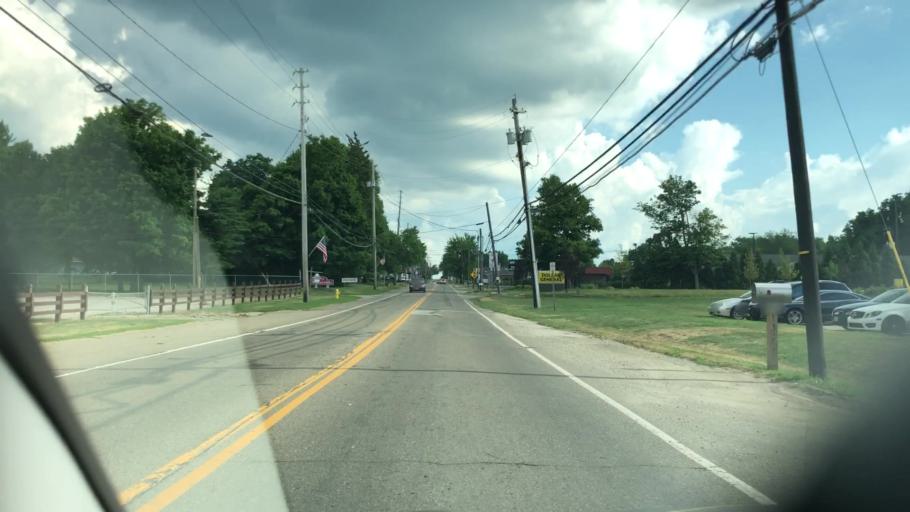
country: US
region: Ohio
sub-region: Summit County
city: Fairlawn
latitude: 41.1022
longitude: -81.6446
